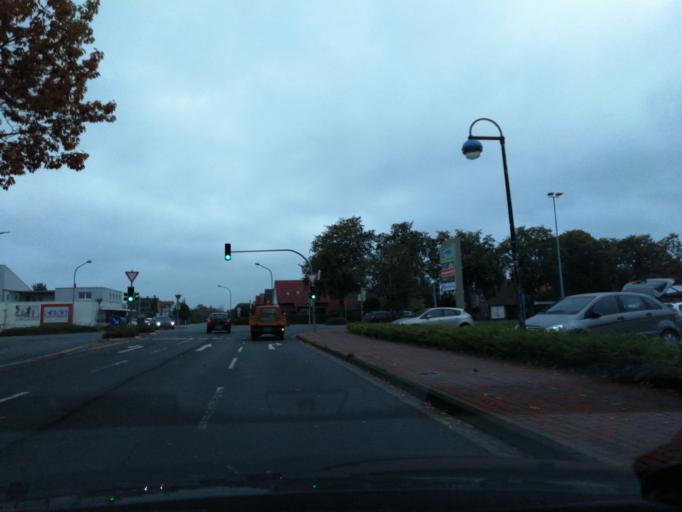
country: DE
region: Lower Saxony
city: Schortens
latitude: 53.5437
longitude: 7.9497
